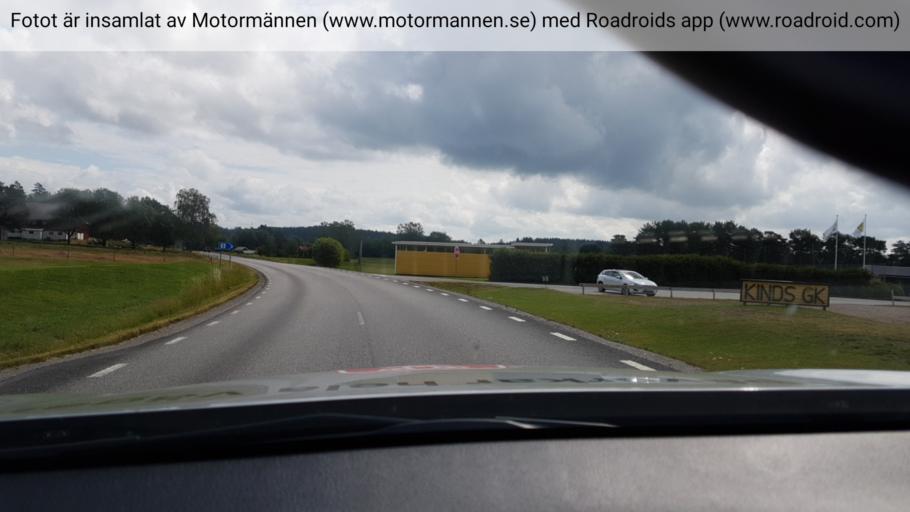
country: SE
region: Vaestra Goetaland
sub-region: Svenljunga Kommun
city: Svenljunga
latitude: 57.4638
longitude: 13.1755
